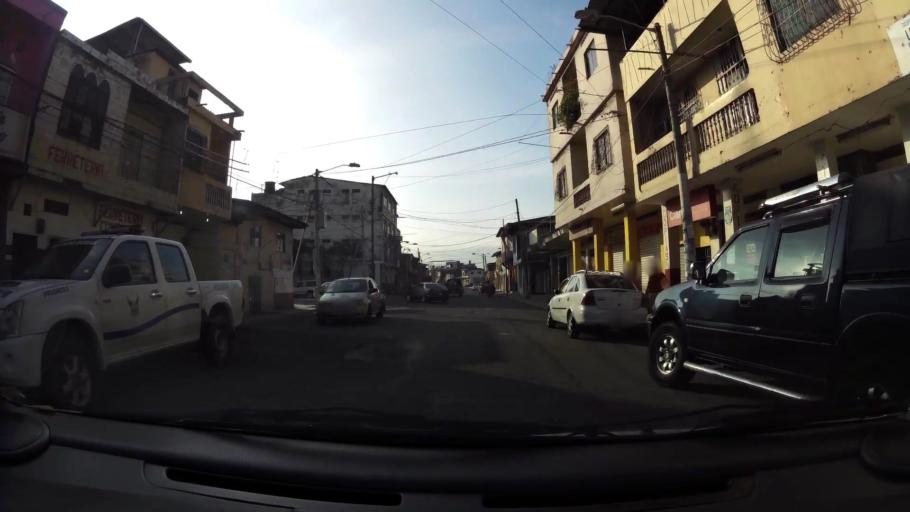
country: EC
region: Guayas
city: Eloy Alfaro
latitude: -2.1699
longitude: -79.8491
